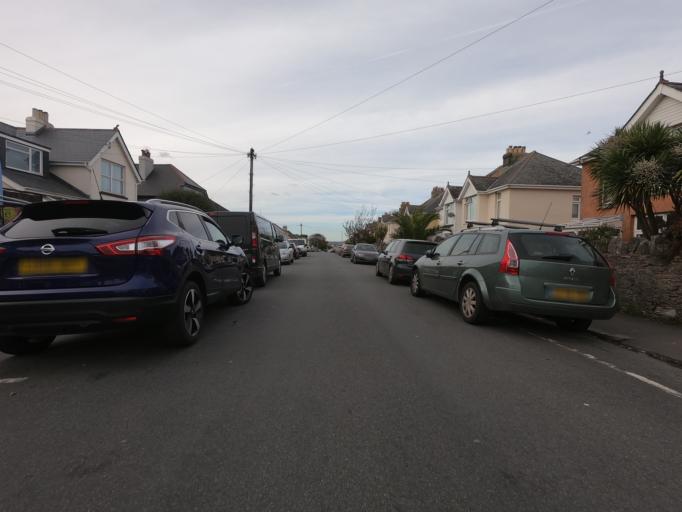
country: GB
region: England
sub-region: Borough of Torbay
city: Brixham
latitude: 50.3941
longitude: -3.5077
